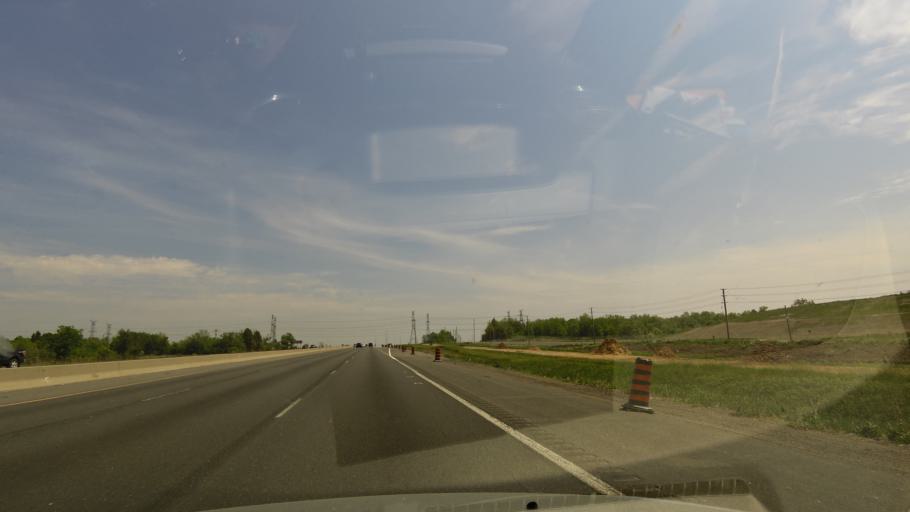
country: CA
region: Ontario
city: Oshawa
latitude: 43.8821
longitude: -78.7366
